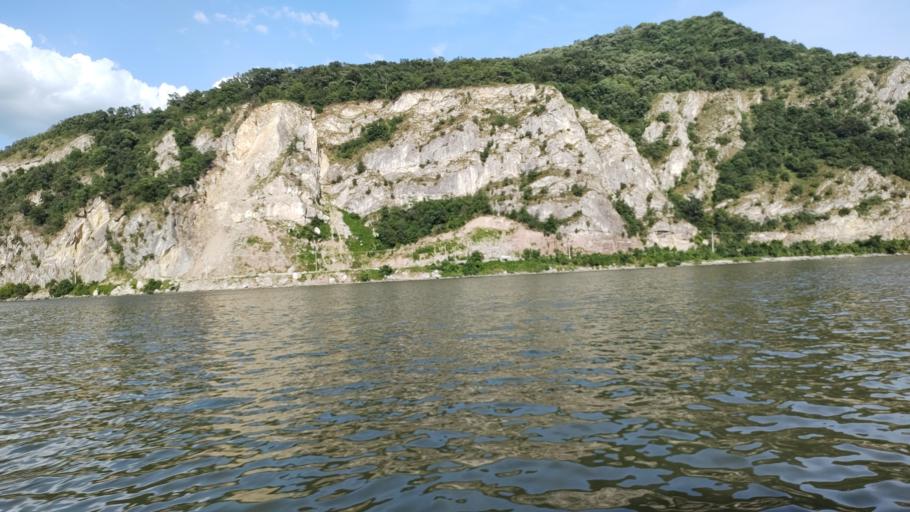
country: RO
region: Caras-Severin
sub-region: Comuna Berzasca
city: Berzasca
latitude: 44.6136
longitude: 22.0027
